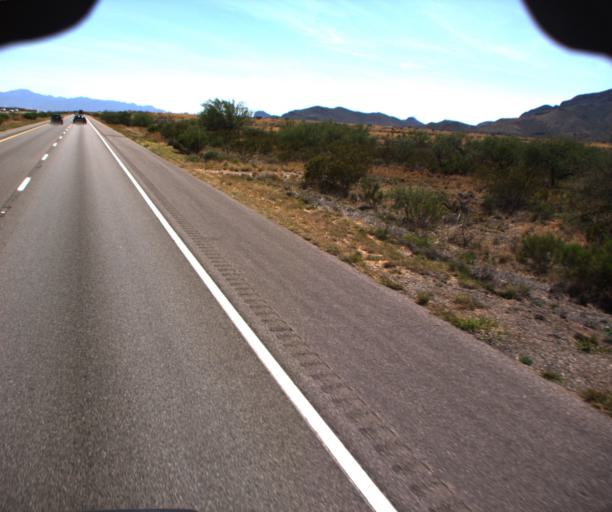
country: US
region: Arizona
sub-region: Cochise County
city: Whetstone
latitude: 31.8126
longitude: -110.3484
